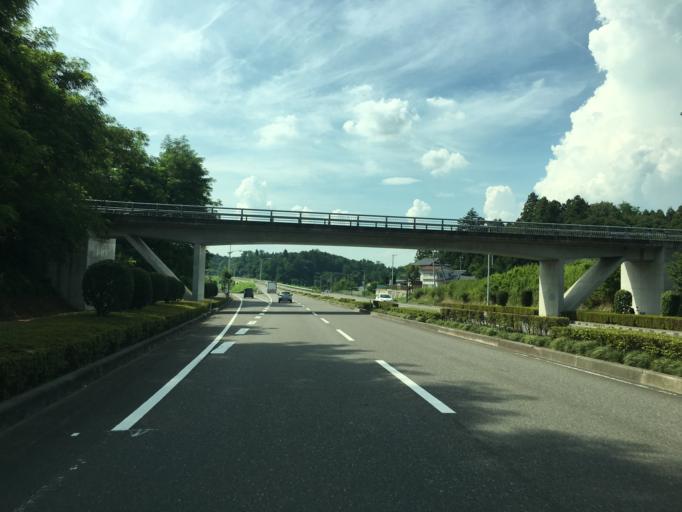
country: JP
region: Fukushima
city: Sukagawa
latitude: 37.2611
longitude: 140.4189
